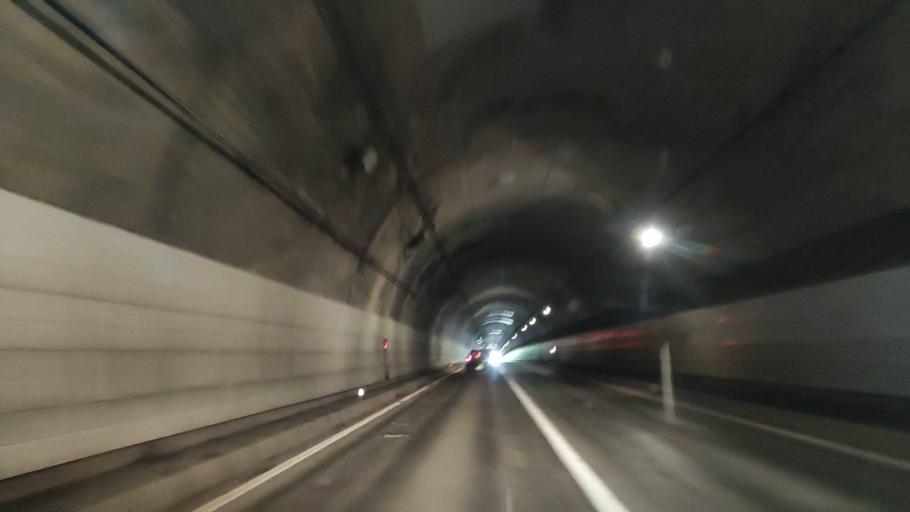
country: JP
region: Akita
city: Takanosu
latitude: 40.2132
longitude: 140.2189
